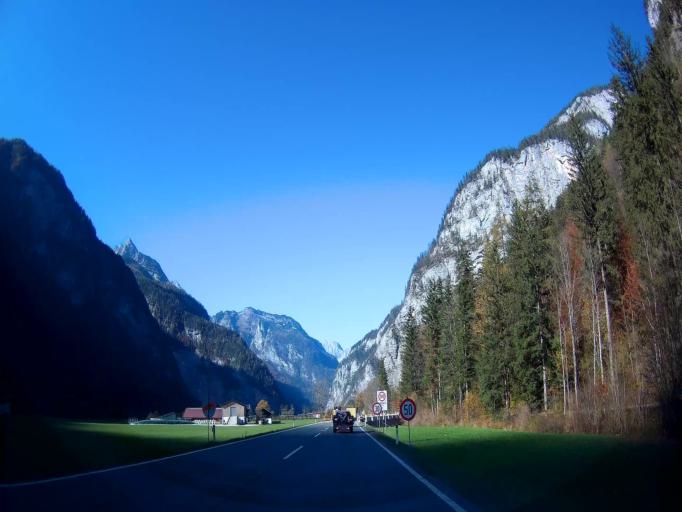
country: AT
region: Salzburg
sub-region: Politischer Bezirk Zell am See
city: Leogang
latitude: 47.4938
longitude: 12.8085
